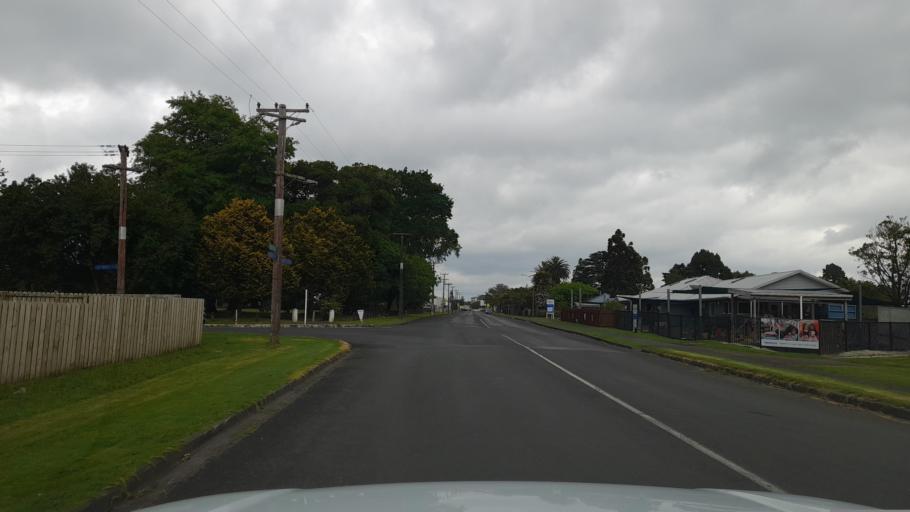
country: NZ
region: Northland
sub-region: Far North District
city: Waimate North
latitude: -35.4050
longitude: 173.7963
